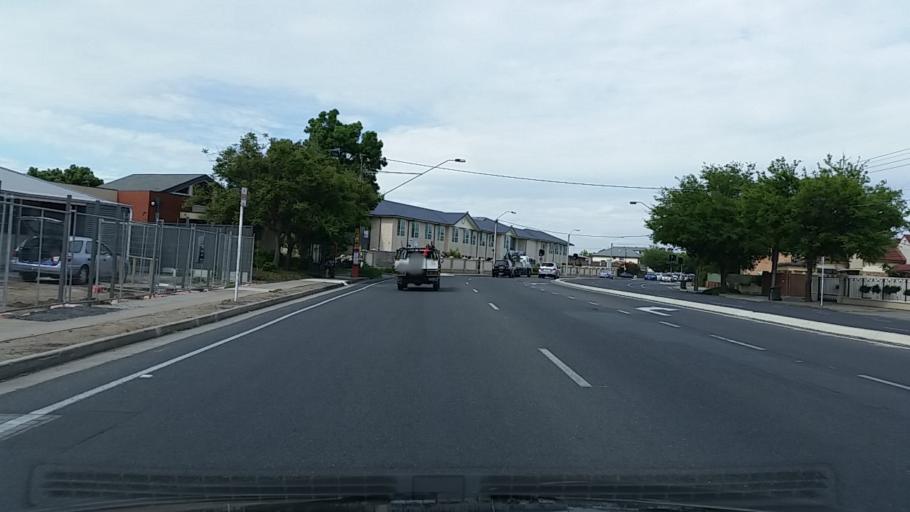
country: AU
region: South Australia
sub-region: City of West Torrens
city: Thebarton
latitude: -34.9253
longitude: 138.5424
